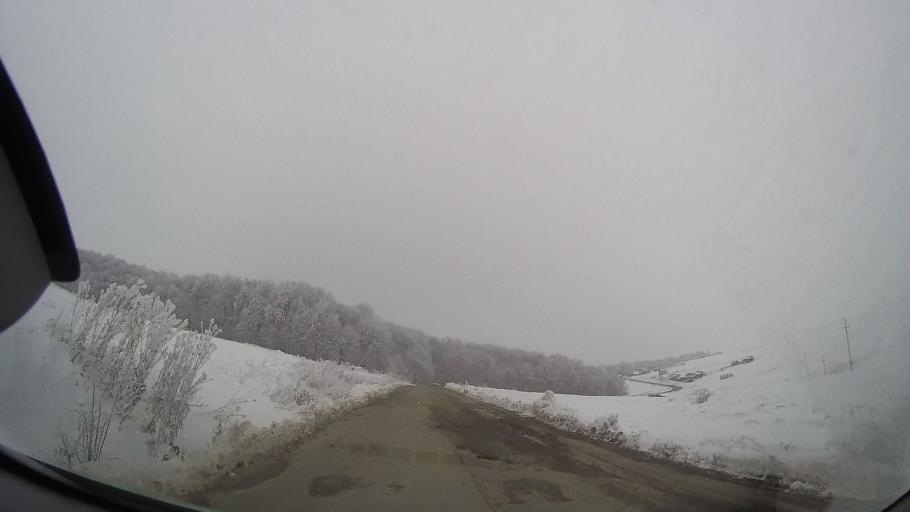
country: RO
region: Neamt
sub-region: Comuna Pancesti
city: Pancesti
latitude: 46.9151
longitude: 27.1627
